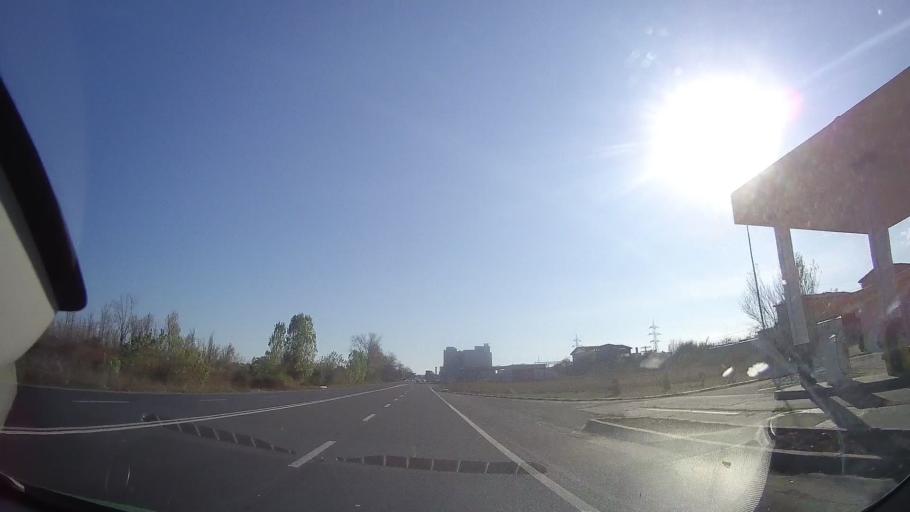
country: RO
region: Constanta
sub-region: Municipiul Mangalia
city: Mangalia
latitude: 43.8336
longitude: 28.5780
